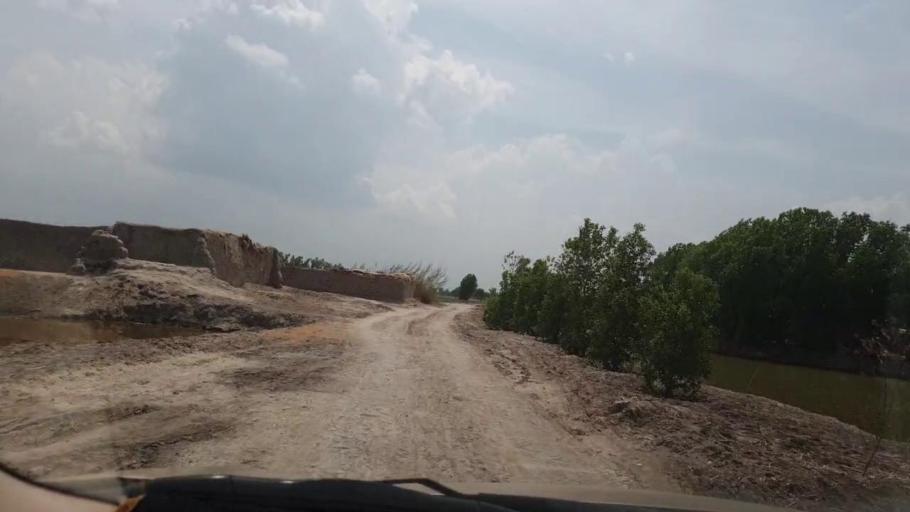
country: PK
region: Sindh
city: Larkana
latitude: 27.6163
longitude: 68.1546
